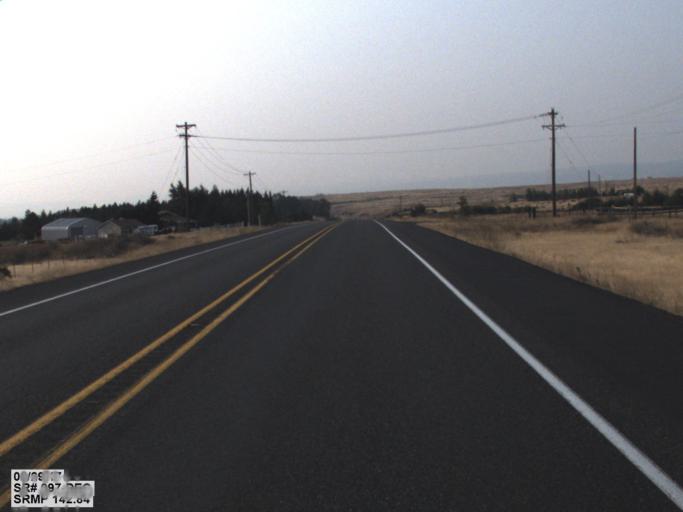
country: US
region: Washington
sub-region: Kittitas County
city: Ellensburg
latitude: 47.1137
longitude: -120.6663
